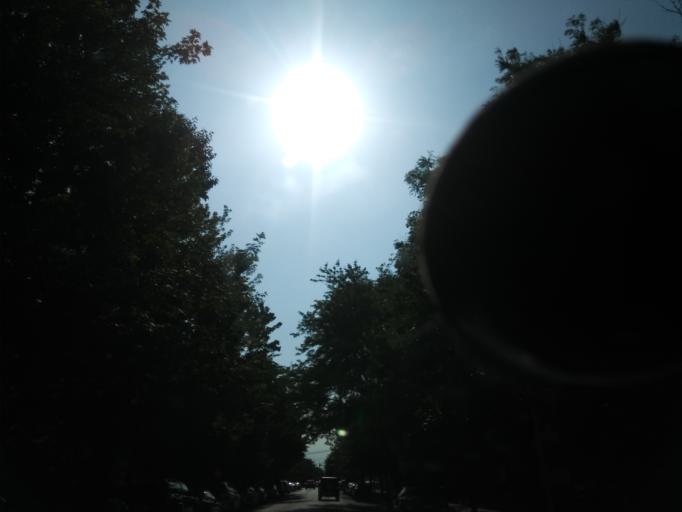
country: US
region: Illinois
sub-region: Cook County
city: Chicago
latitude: 41.8790
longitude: -87.6649
